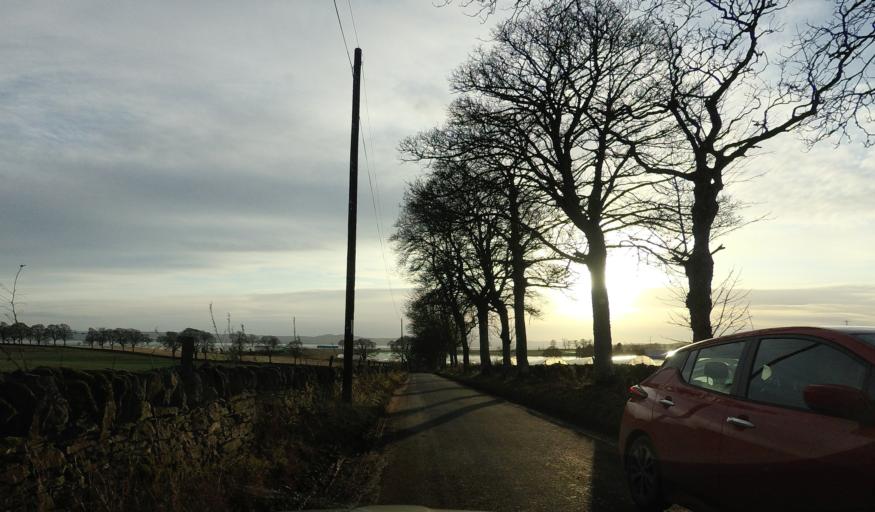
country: GB
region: Scotland
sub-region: Angus
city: Muirhead
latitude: 56.4995
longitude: -3.1124
